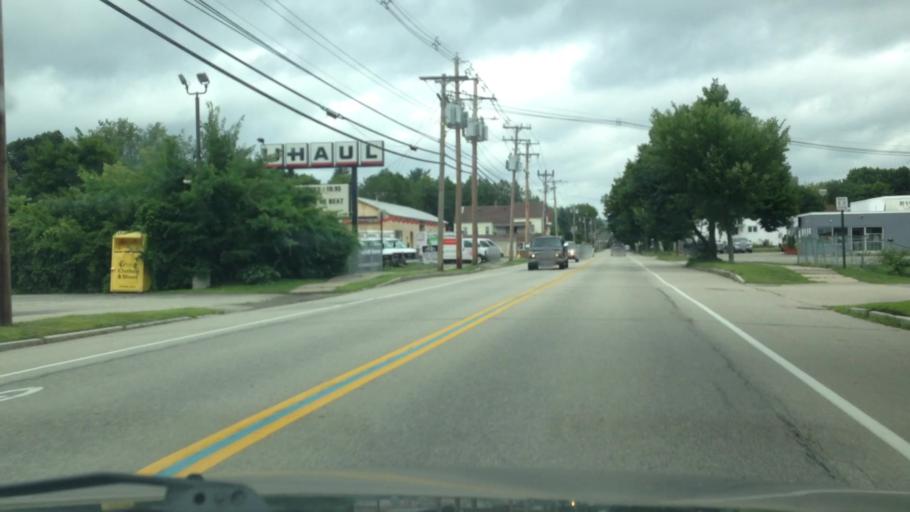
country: US
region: New Hampshire
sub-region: Cheshire County
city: Keene
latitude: 42.9259
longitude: -72.2699
